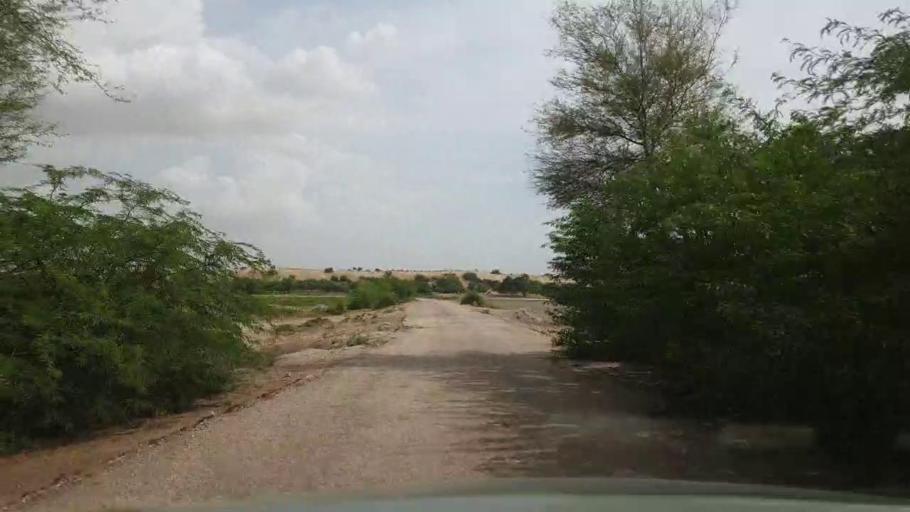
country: PK
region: Sindh
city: Bozdar
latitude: 27.0793
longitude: 69.0136
